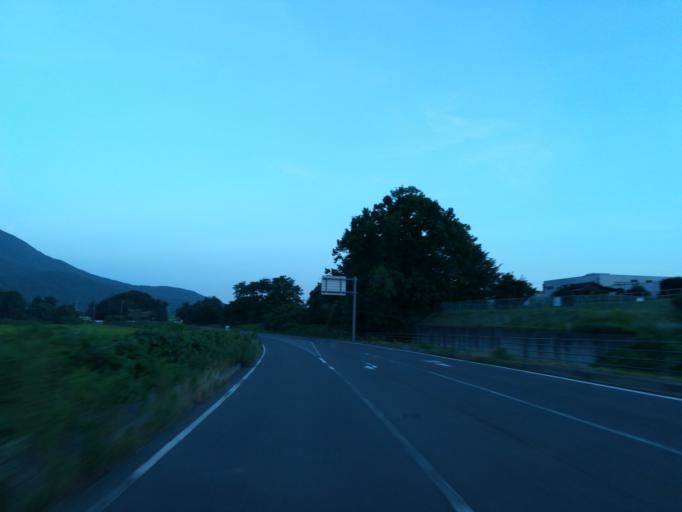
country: JP
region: Ibaraki
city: Makabe
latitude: 36.2637
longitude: 140.0587
